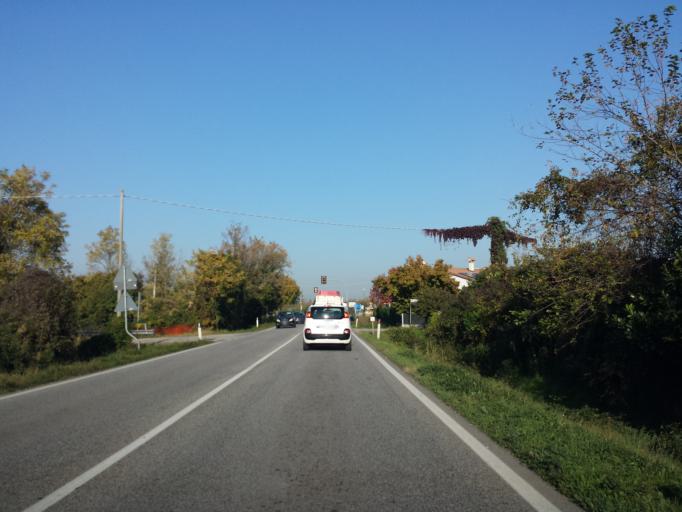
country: IT
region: Veneto
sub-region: Provincia di Treviso
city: Caselle
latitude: 45.7419
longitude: 11.9690
